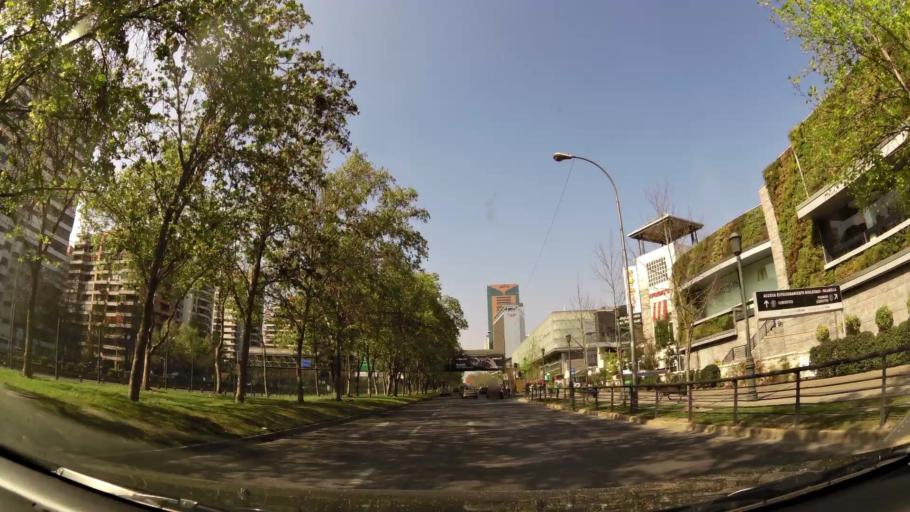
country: CL
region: Santiago Metropolitan
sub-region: Provincia de Santiago
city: Villa Presidente Frei, Nunoa, Santiago, Chile
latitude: -33.4017
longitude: -70.5796
